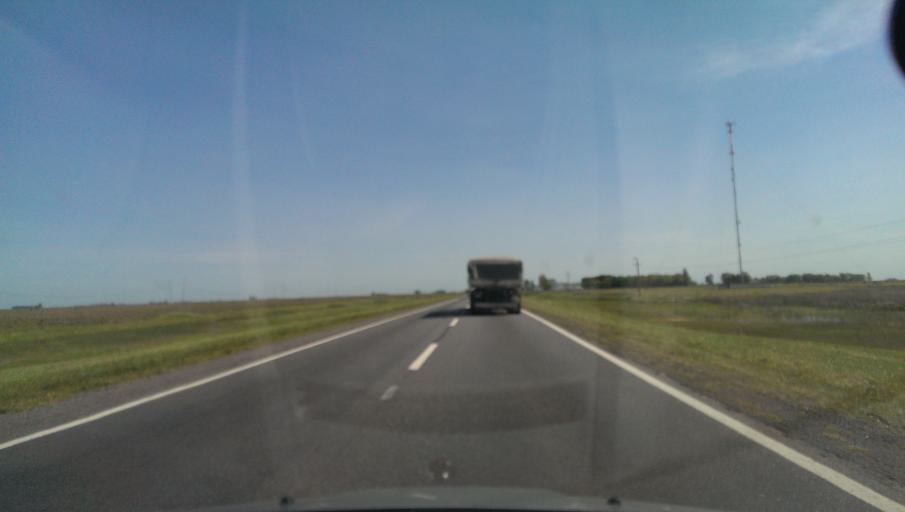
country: AR
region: Buenos Aires
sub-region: Partido de Azul
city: Azul
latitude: -36.6050
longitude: -59.6707
